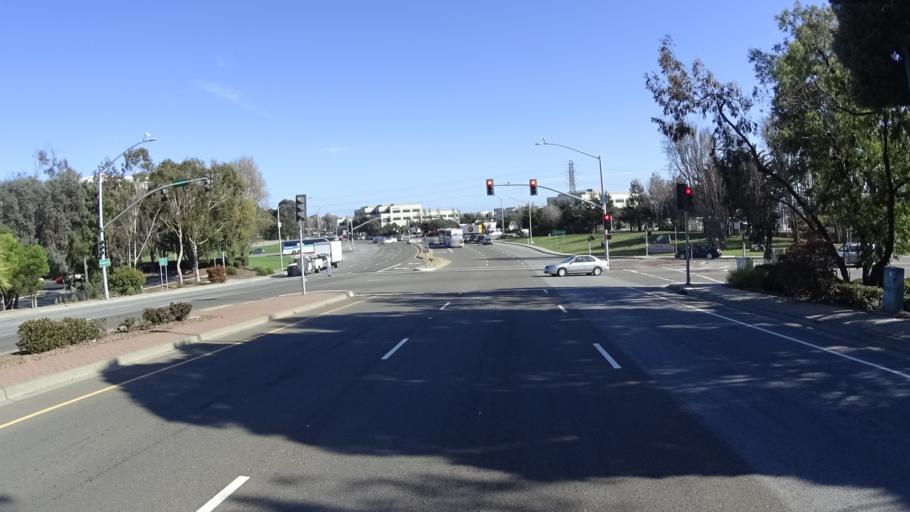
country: US
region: California
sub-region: San Mateo County
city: South San Francisco
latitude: 37.6551
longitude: -122.4038
